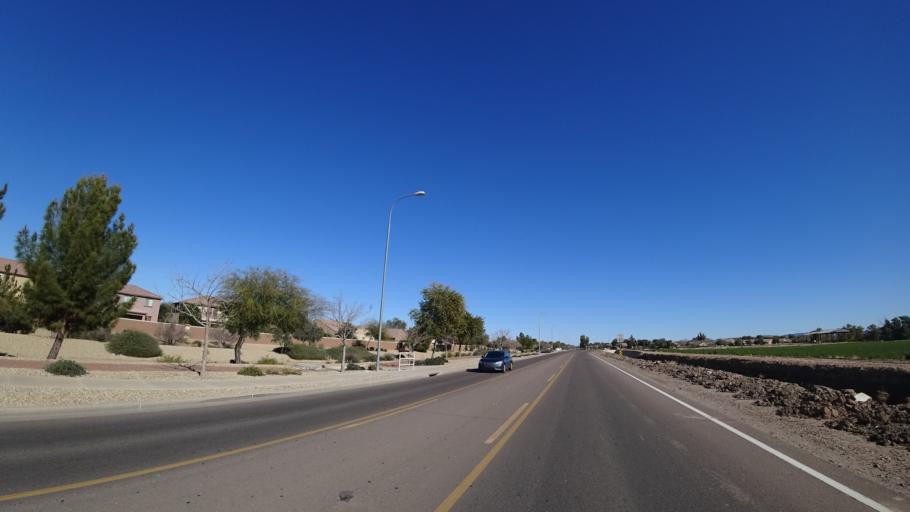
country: US
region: Arizona
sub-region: Maricopa County
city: Tolleson
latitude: 33.4211
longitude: -112.2836
